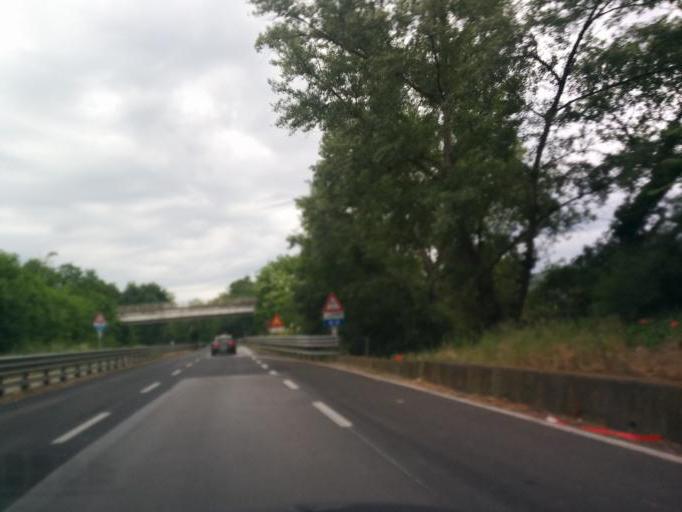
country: IT
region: Tuscany
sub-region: Provincia di Siena
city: Castellina Scalo
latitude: 43.3962
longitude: 11.2011
